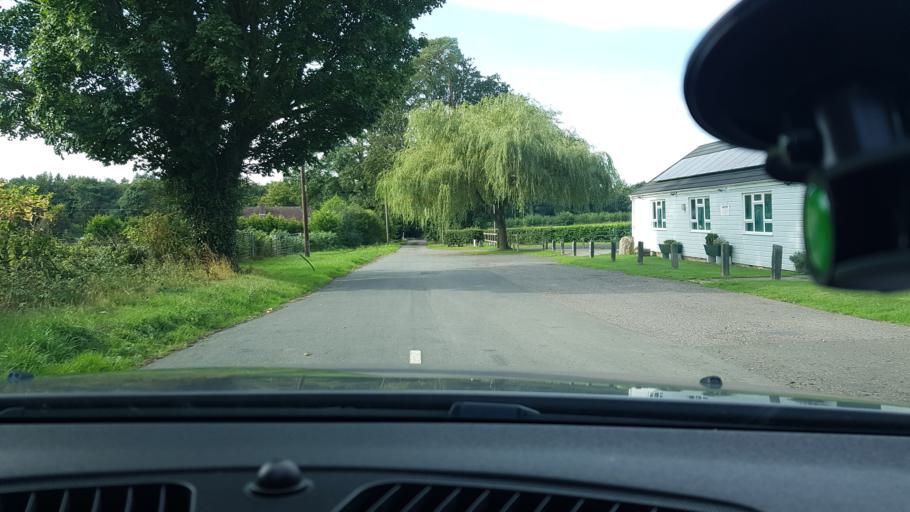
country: GB
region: England
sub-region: West Berkshire
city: Lambourn
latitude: 51.4722
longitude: -1.5179
